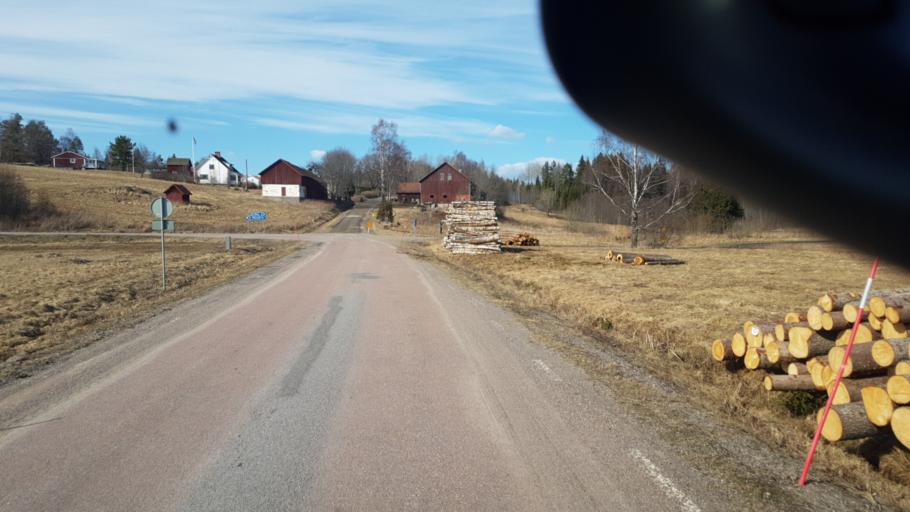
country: SE
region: Vaermland
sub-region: Eda Kommun
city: Amotfors
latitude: 59.8308
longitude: 12.3582
